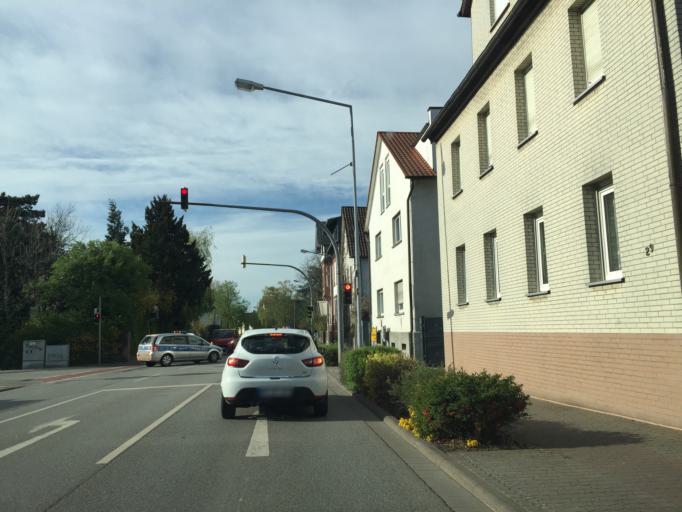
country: DE
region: Hesse
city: Zwingenberg
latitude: 49.7264
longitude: 8.6120
